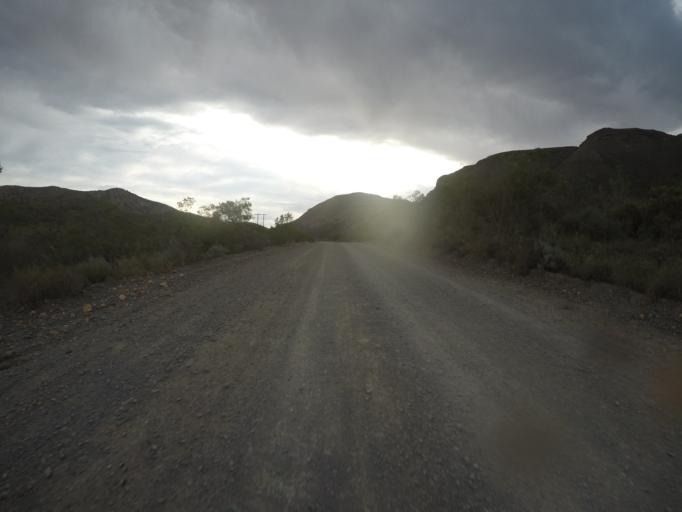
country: ZA
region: Eastern Cape
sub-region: Cacadu District Municipality
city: Willowmore
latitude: -33.5169
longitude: 23.8261
